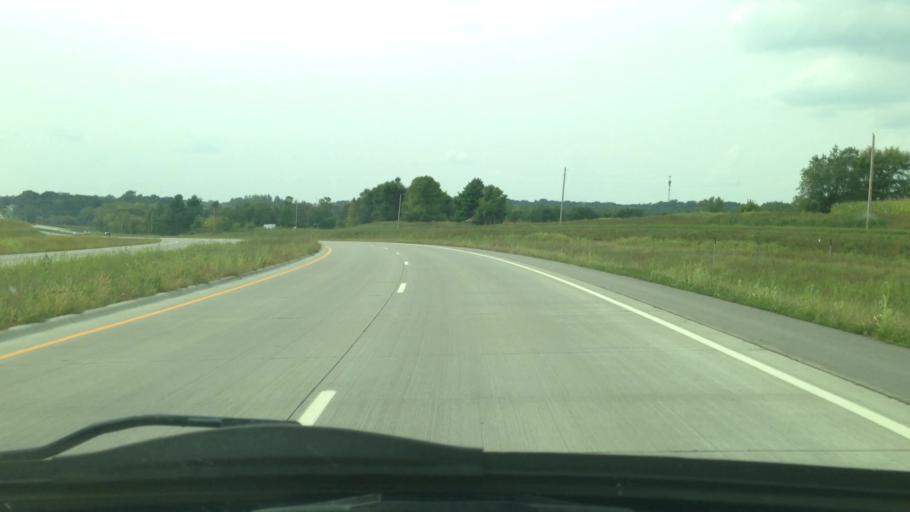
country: US
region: Minnesota
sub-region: Olmsted County
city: Rochester
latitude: 44.0794
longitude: -92.4618
